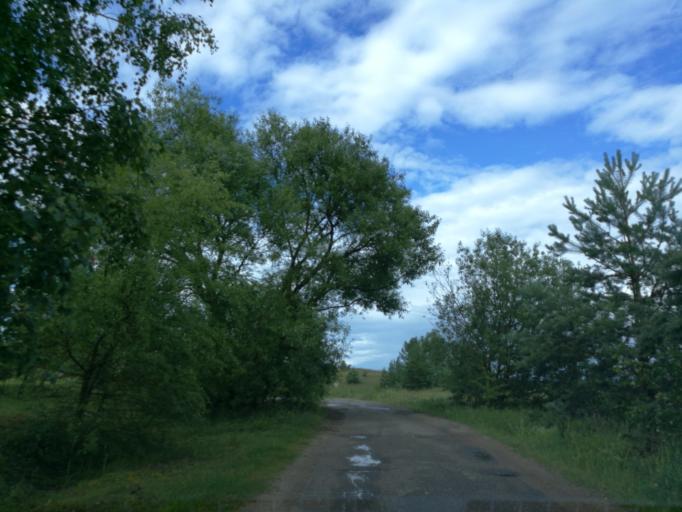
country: LT
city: Lentvaris
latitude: 54.6753
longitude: 25.0202
